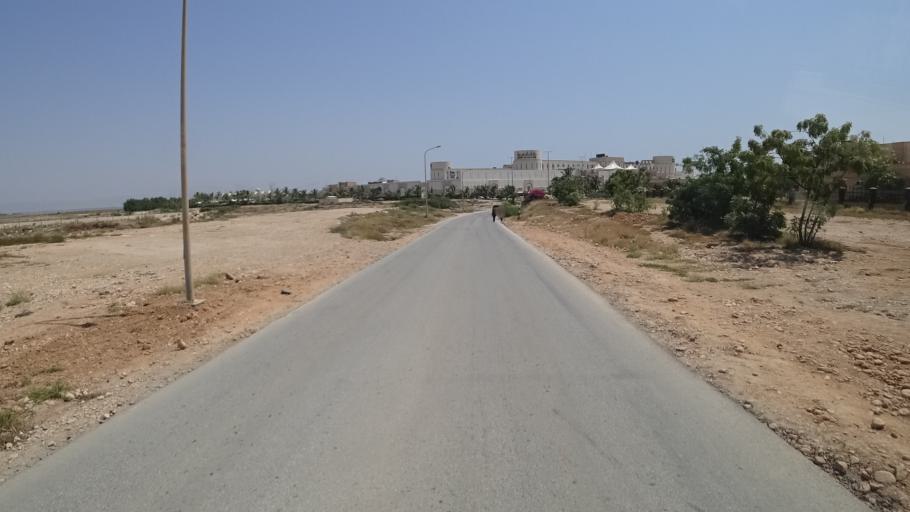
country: OM
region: Zufar
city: Salalah
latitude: 17.0239
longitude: 54.0619
